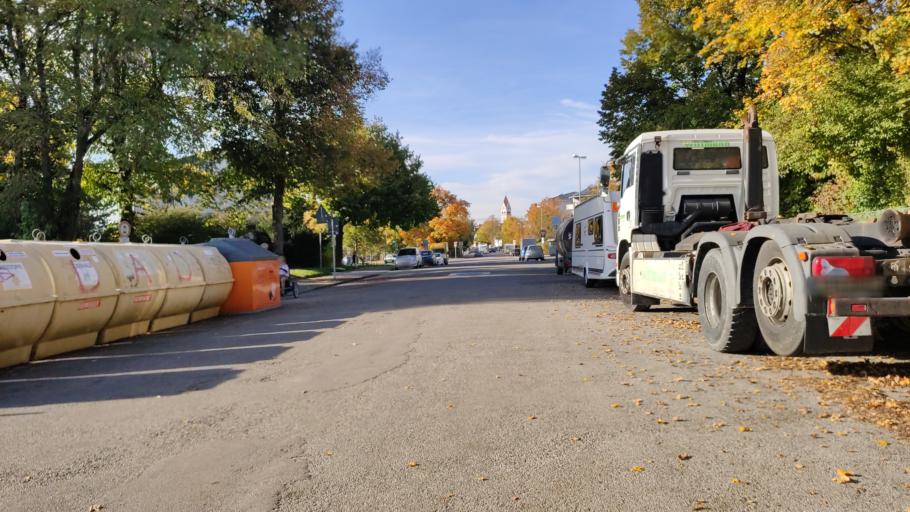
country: DE
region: Bavaria
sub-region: Upper Bavaria
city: Pasing
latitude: 48.1397
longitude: 11.4687
